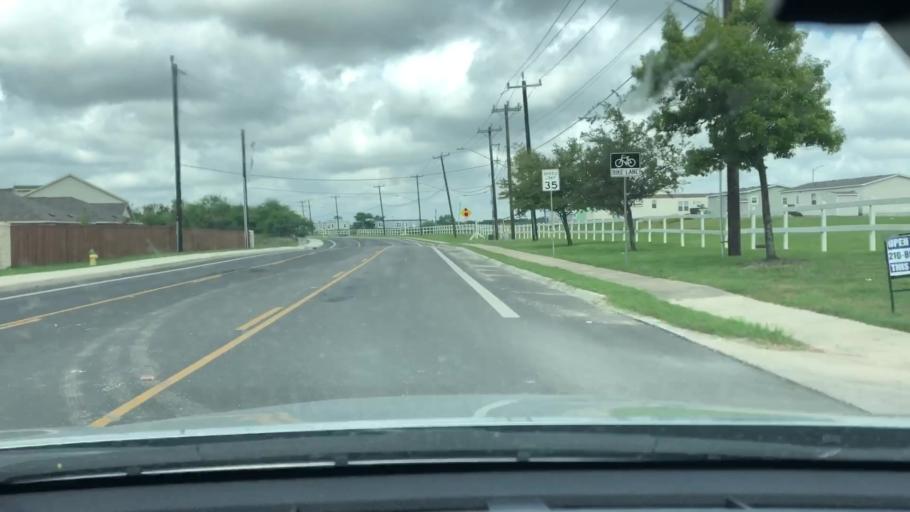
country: US
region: Texas
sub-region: Bexar County
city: Windcrest
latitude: 29.4954
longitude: -98.3610
